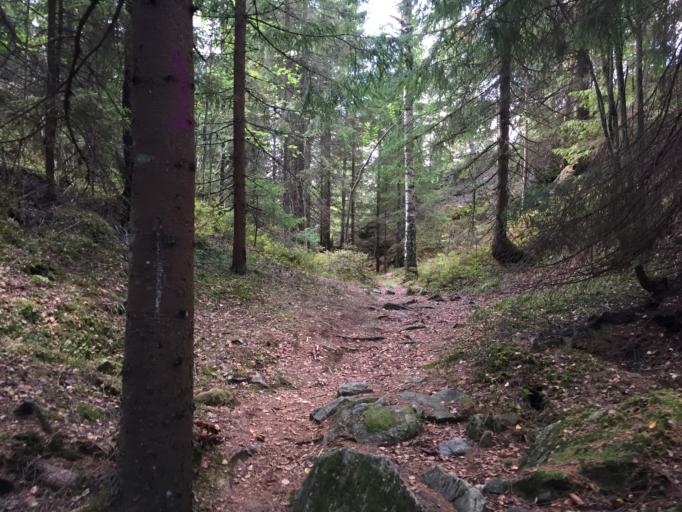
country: NO
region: Akershus
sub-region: Skedsmo
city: Lillestrom
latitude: 59.9240
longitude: 11.0164
